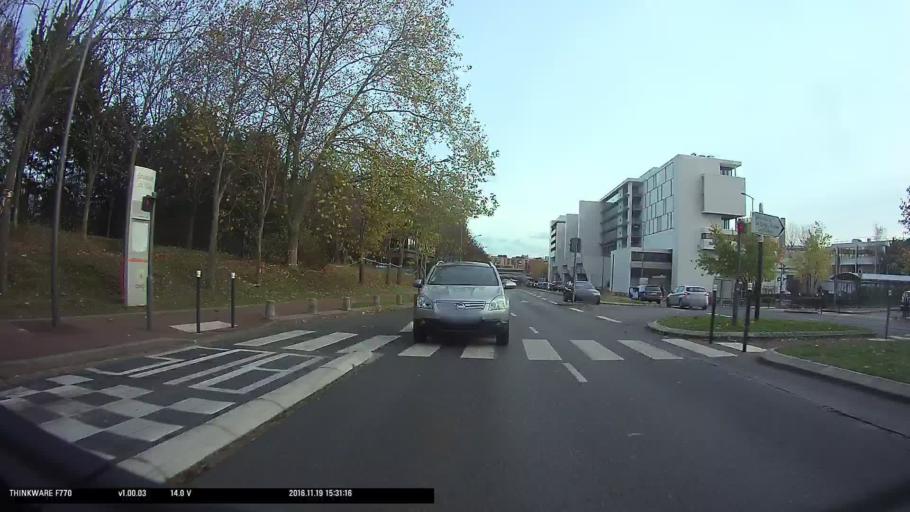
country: FR
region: Ile-de-France
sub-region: Departement du Val-d'Oise
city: Cergy-Pontoise
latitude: 49.0411
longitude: 2.0740
